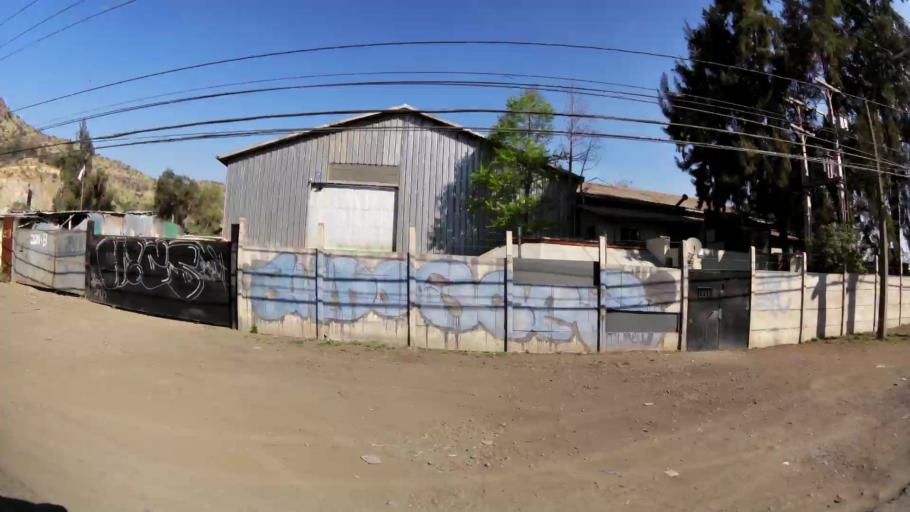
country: CL
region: Santiago Metropolitan
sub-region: Provincia de Chacabuco
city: Chicureo Abajo
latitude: -33.3414
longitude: -70.6964
